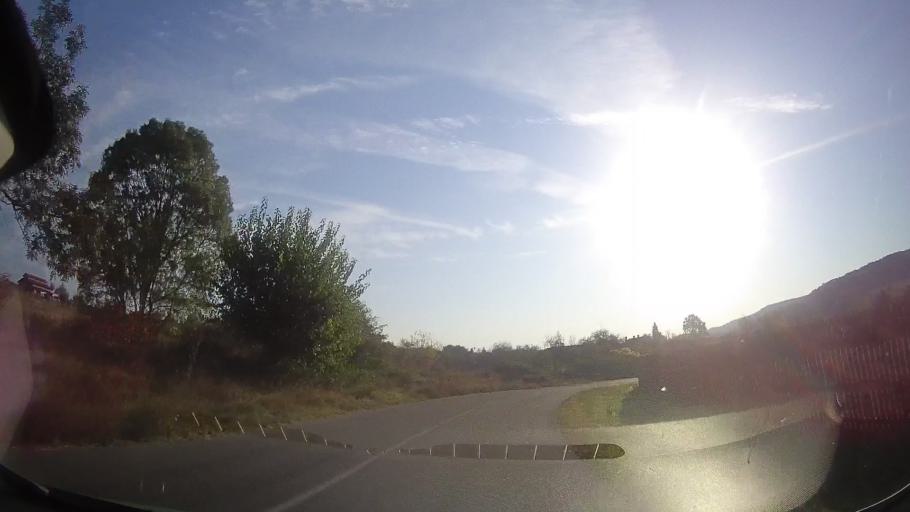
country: RO
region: Timis
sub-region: Comuna Bogda
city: Bogda
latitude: 45.9824
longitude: 21.5493
